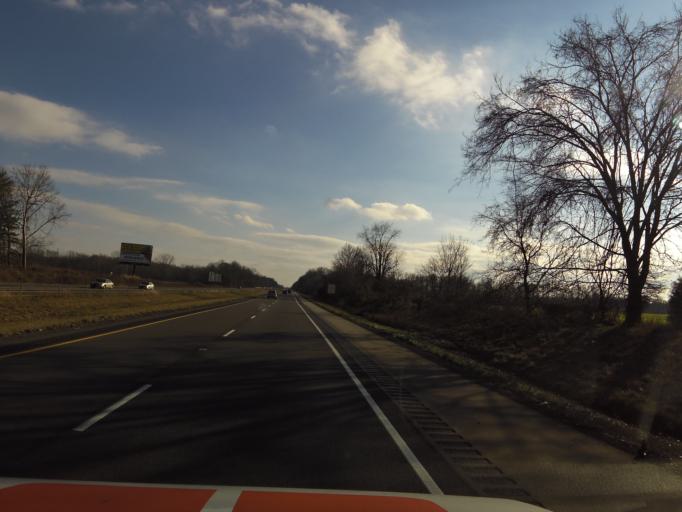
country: US
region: Indiana
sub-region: Scott County
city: Austin
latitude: 38.7700
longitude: -85.8335
